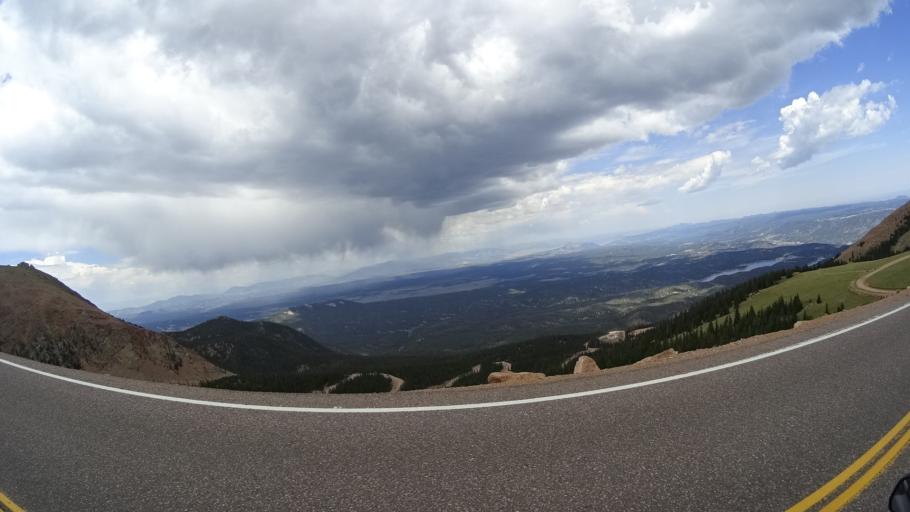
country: US
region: Colorado
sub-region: El Paso County
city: Cascade-Chipita Park
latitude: 38.8749
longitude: -105.0672
